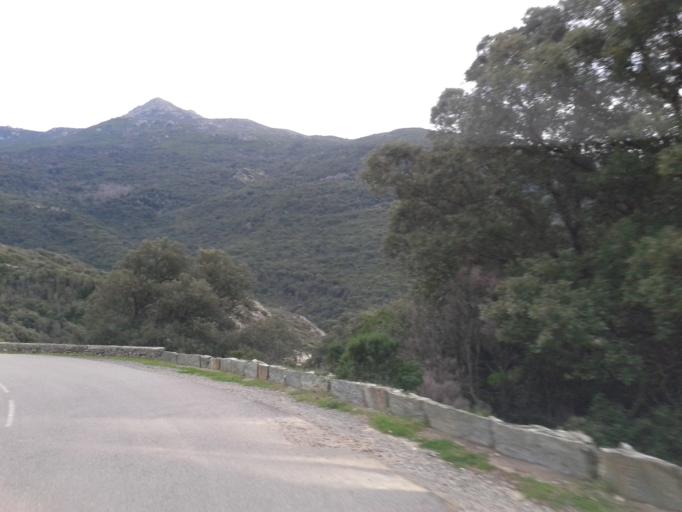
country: FR
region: Corsica
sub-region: Departement de la Haute-Corse
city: Brando
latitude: 42.8692
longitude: 9.3480
